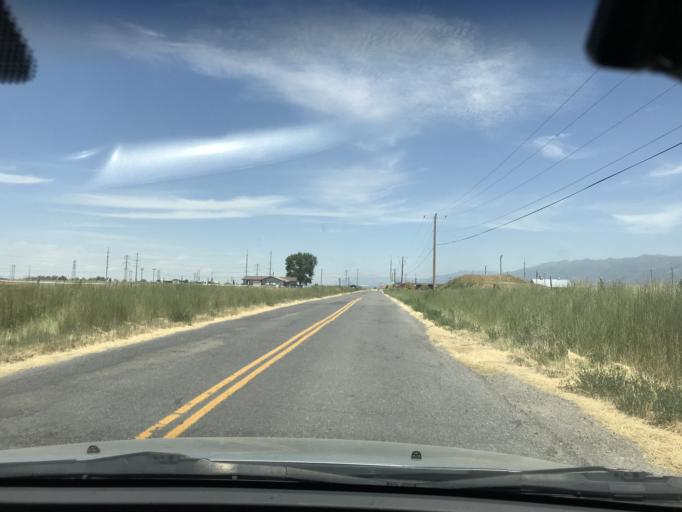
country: US
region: Utah
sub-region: Davis County
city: North Salt Lake
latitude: 40.8388
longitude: -111.9551
